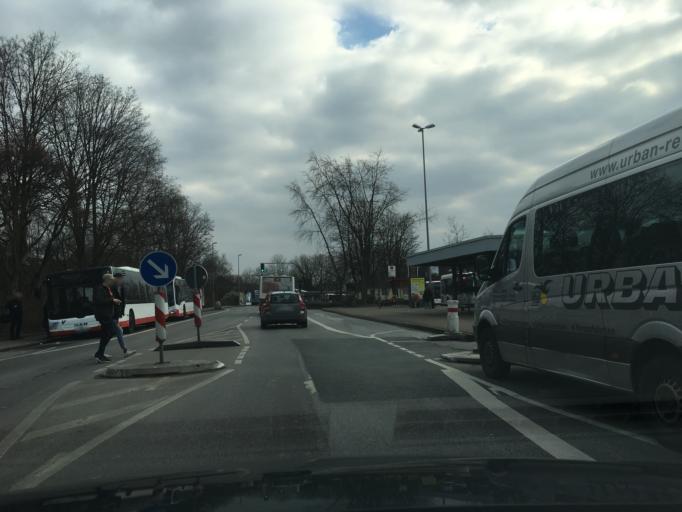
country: DE
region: North Rhine-Westphalia
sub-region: Regierungsbezirk Munster
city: Gladbeck
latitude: 51.5744
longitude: 6.9960
